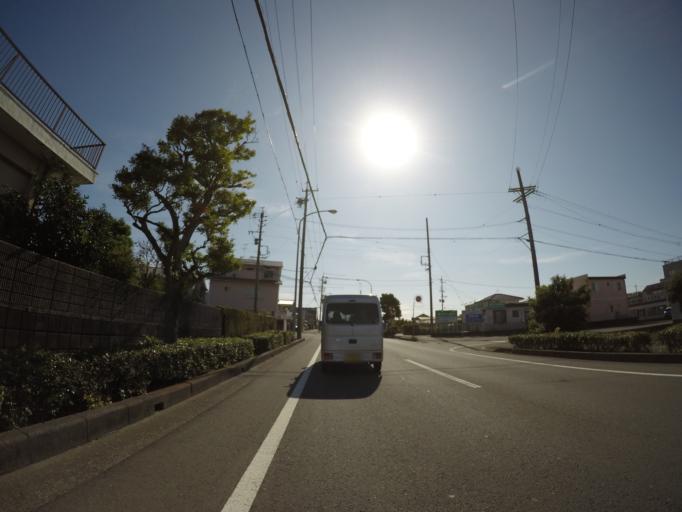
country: JP
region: Shizuoka
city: Shizuoka-shi
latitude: 34.9666
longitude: 138.4232
